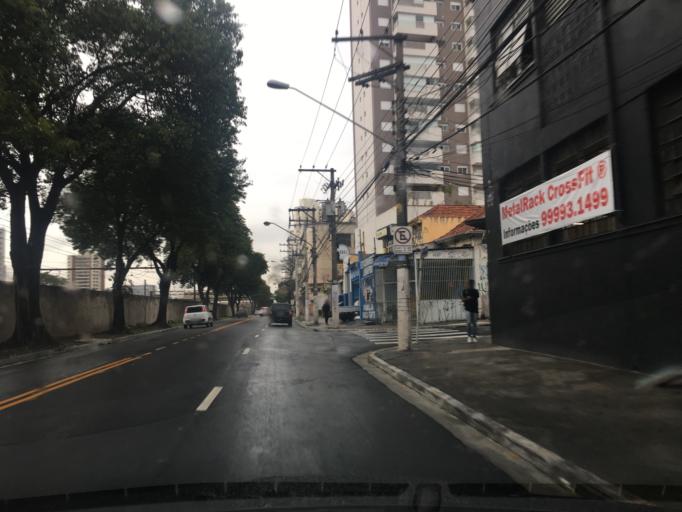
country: BR
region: Sao Paulo
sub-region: Sao Paulo
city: Sao Paulo
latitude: -23.5383
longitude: -46.5685
